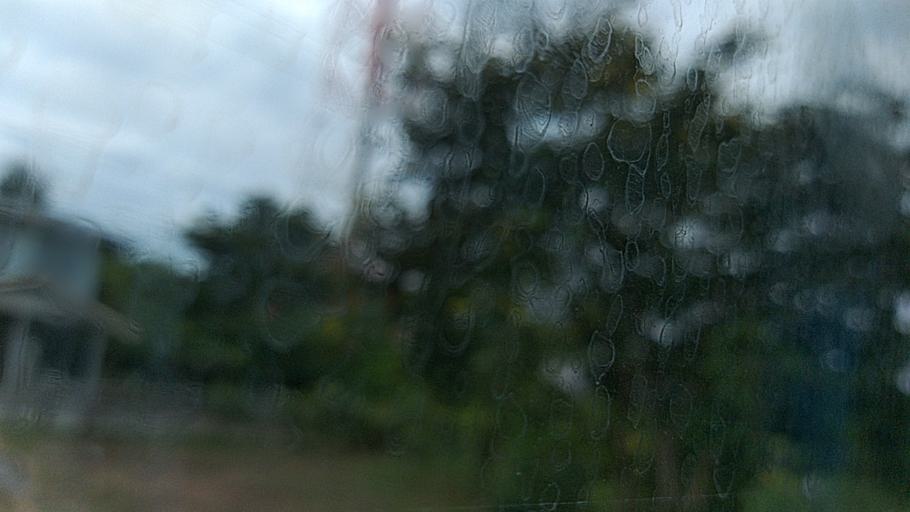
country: TH
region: Kalasin
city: Khong Chai
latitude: 16.1406
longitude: 103.4298
